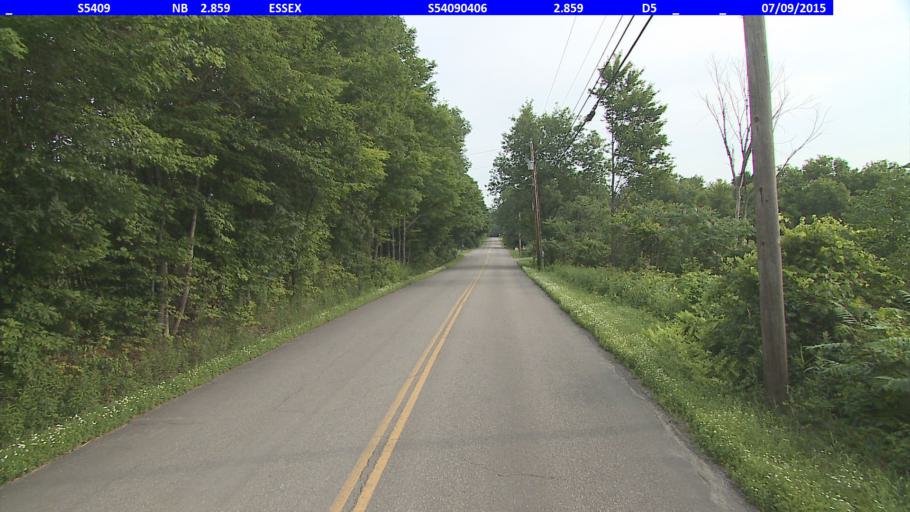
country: US
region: Vermont
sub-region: Chittenden County
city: Essex Junction
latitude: 44.5497
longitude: -73.0703
